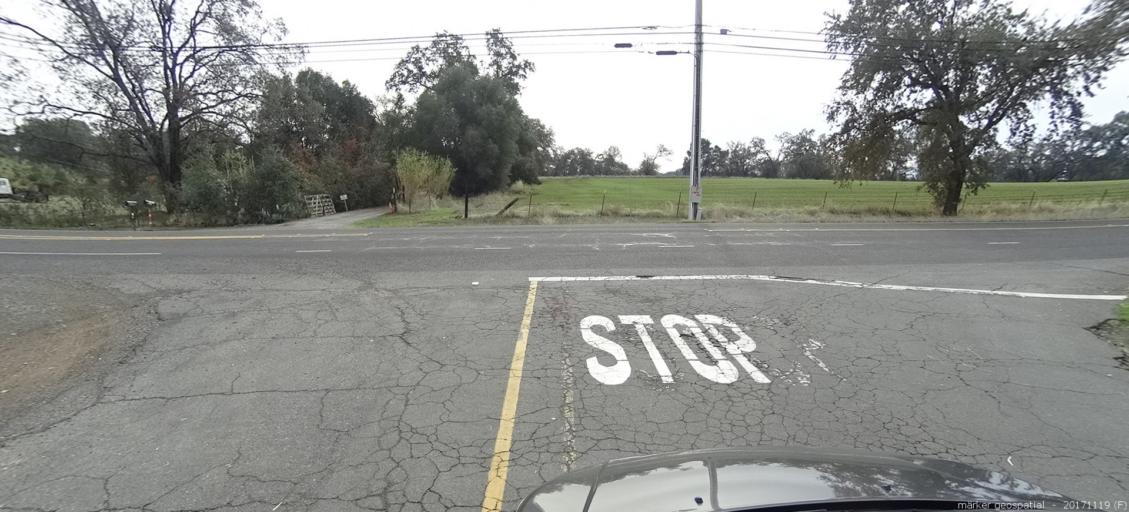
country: US
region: California
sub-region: Shasta County
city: Anderson
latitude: 40.4805
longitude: -122.2838
